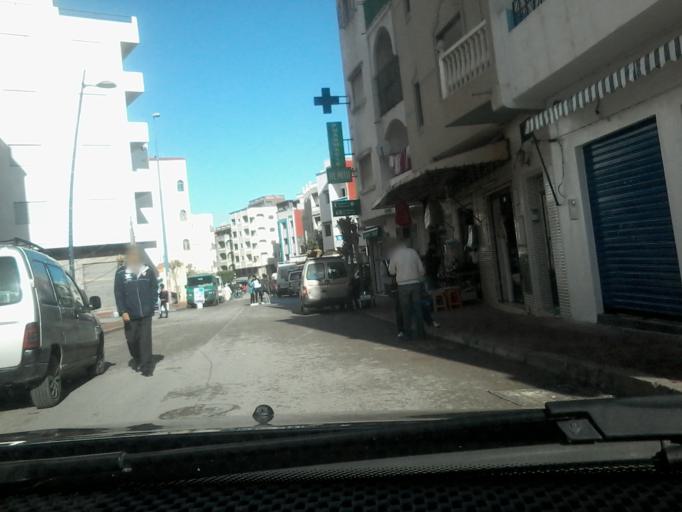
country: MA
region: Tanger-Tetouan
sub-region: Tetouan
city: Martil
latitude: 35.6833
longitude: -5.3262
